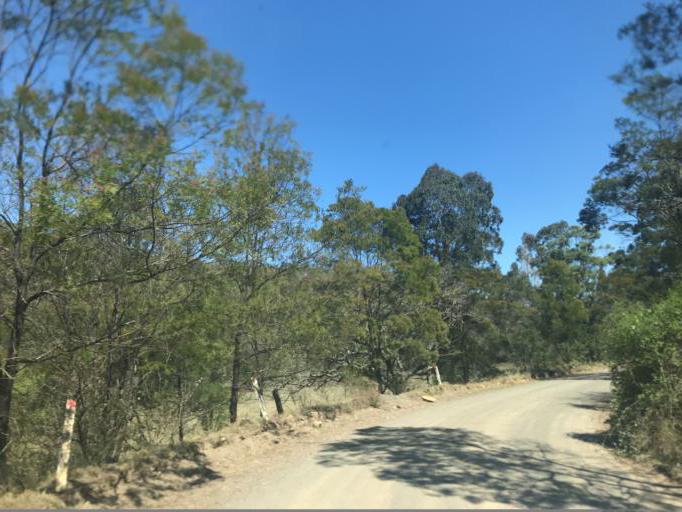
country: AU
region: New South Wales
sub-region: Wyong Shire
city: Little Jilliby
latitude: -33.1958
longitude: 151.0113
